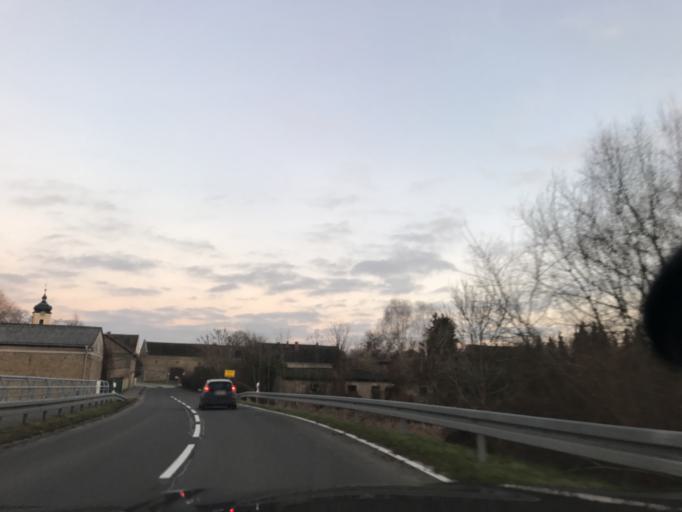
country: DE
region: Brandenburg
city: Pawesin
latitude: 52.5118
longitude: 12.7112
